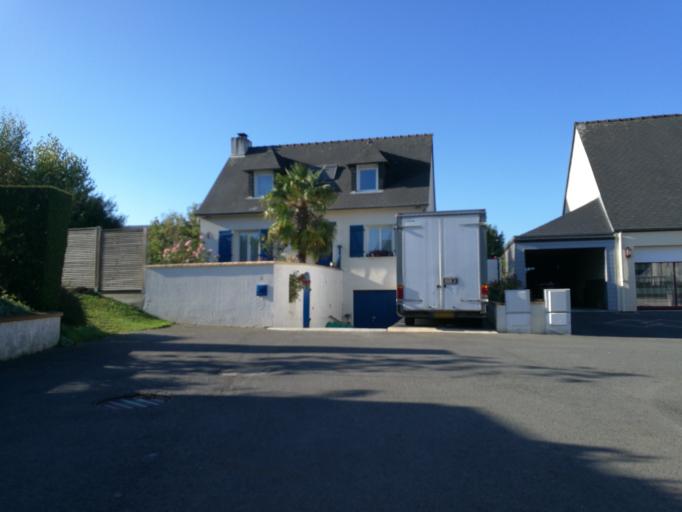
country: FR
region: Brittany
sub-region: Departement d'Ille-et-Vilaine
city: Bedee
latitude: 48.1761
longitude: -1.9414
